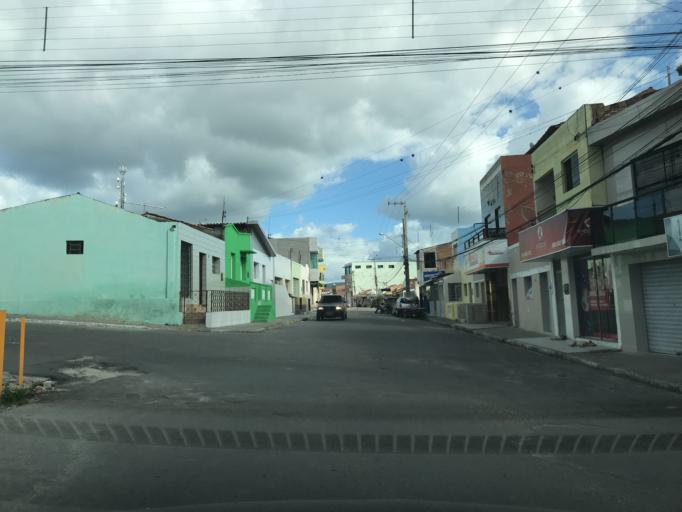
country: BR
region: Pernambuco
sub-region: Bezerros
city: Bezerros
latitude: -8.2405
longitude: -35.7545
